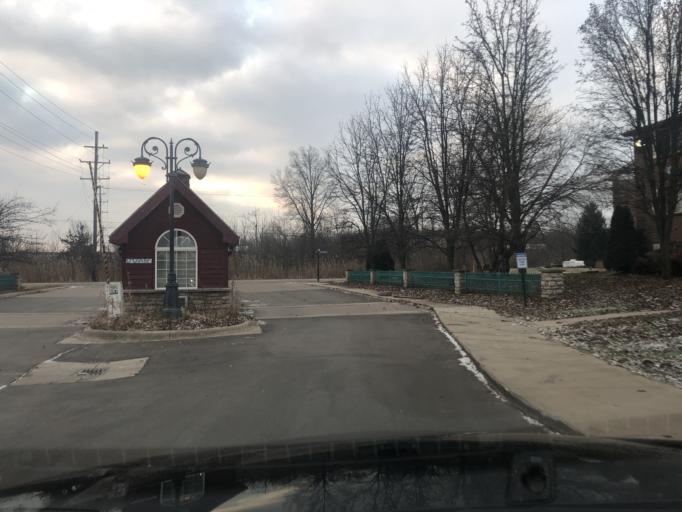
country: US
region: Michigan
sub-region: Wayne County
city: Romulus
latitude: 42.2284
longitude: -83.3897
